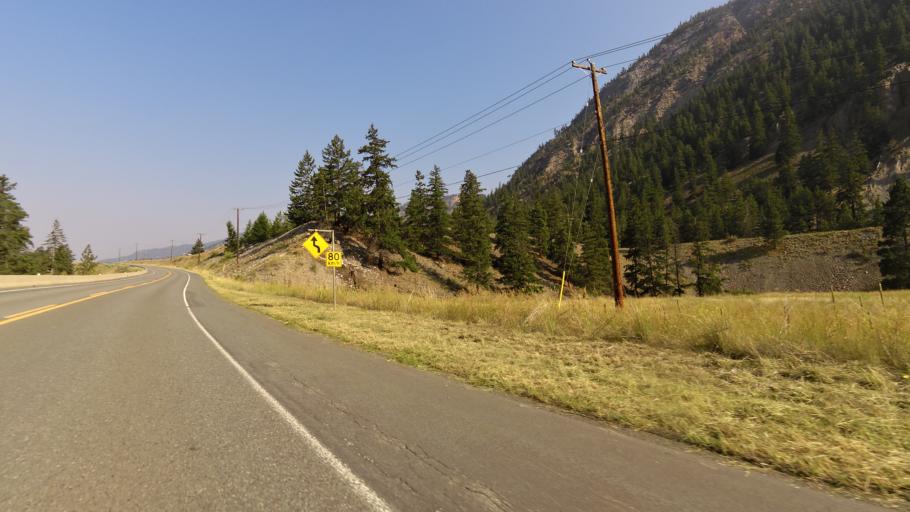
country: CA
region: British Columbia
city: Princeton
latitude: 49.3431
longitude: -120.0650
